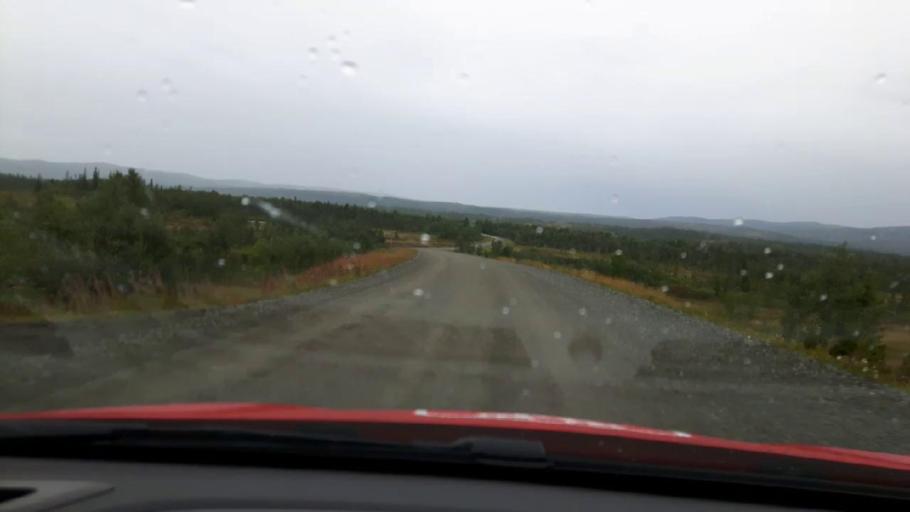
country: NO
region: Nord-Trondelag
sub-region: Meraker
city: Meraker
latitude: 63.5870
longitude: 12.2677
